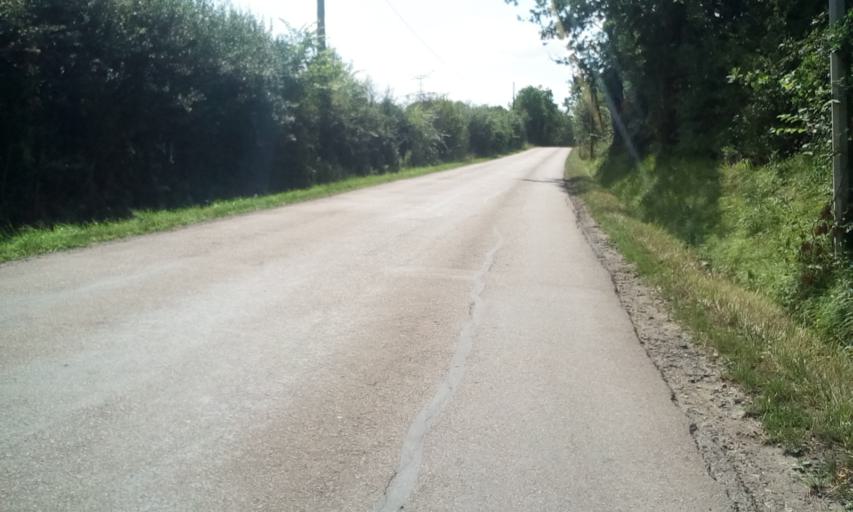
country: FR
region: Lower Normandy
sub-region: Departement du Calvados
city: Argences
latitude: 49.1389
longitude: -0.1559
